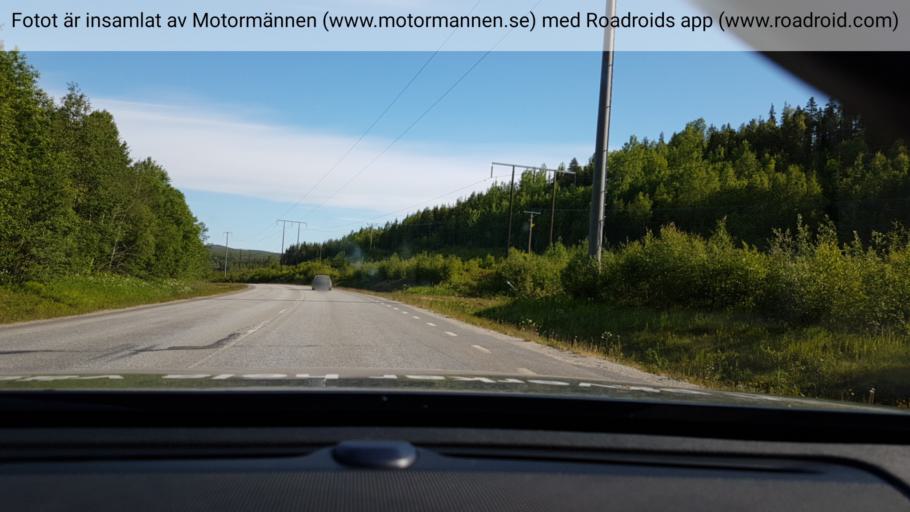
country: SE
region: Vaesterbotten
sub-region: Vannas Kommun
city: Vaennaes
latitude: 63.9894
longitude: 19.7324
